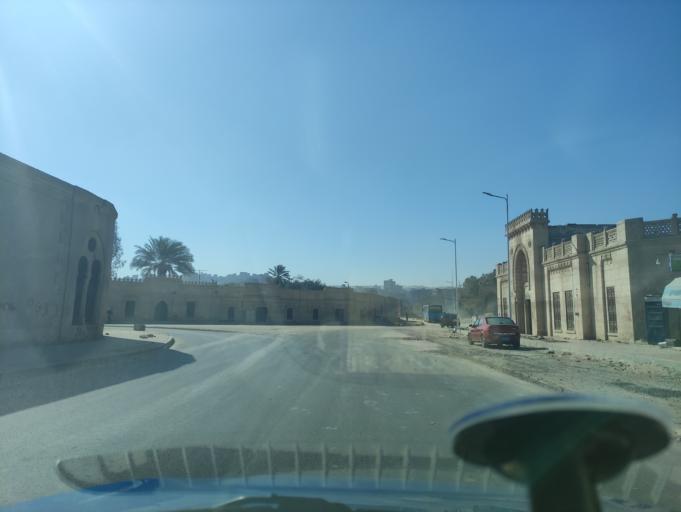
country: EG
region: Muhafazat al Qahirah
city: Cairo
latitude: 30.0533
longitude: 31.2802
